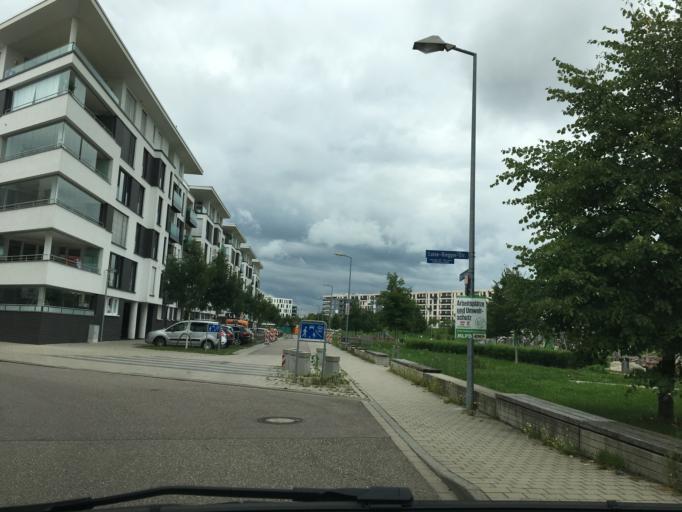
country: DE
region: Baden-Wuerttemberg
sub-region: Karlsruhe Region
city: Karlsruhe
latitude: 49.0017
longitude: 8.4207
